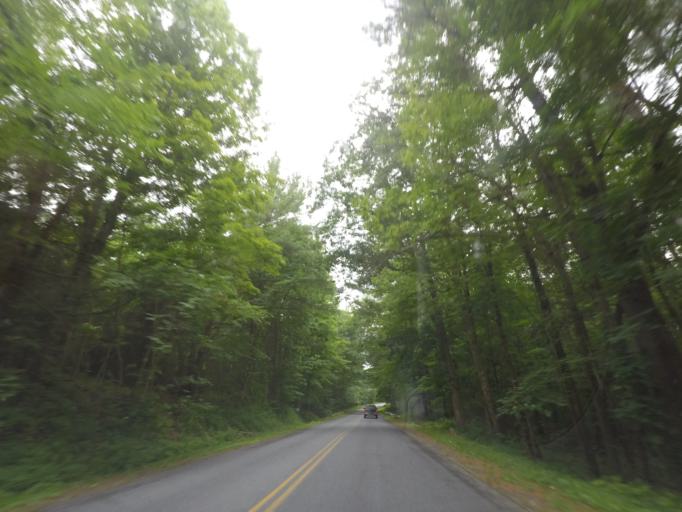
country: US
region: New York
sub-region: Saratoga County
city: Stillwater
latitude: 42.8515
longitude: -73.5441
